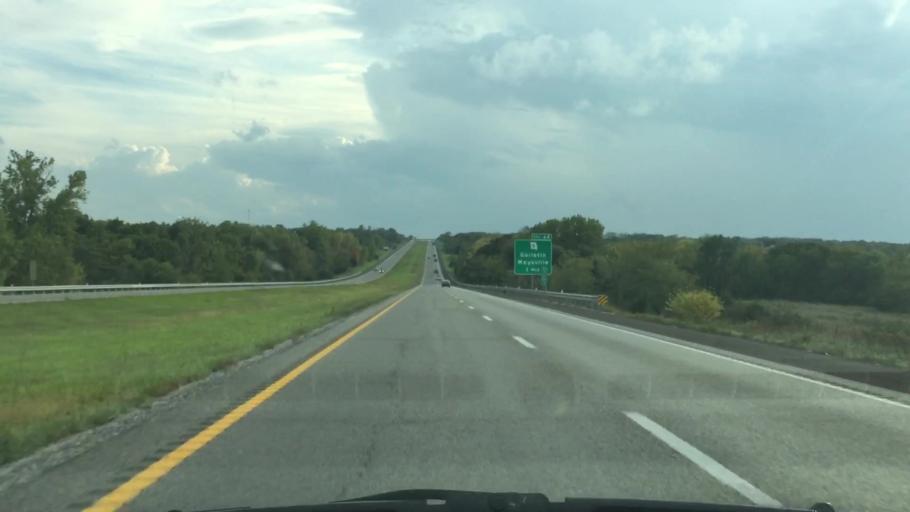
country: US
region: Missouri
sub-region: Daviess County
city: Gallatin
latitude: 39.9170
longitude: -94.1423
